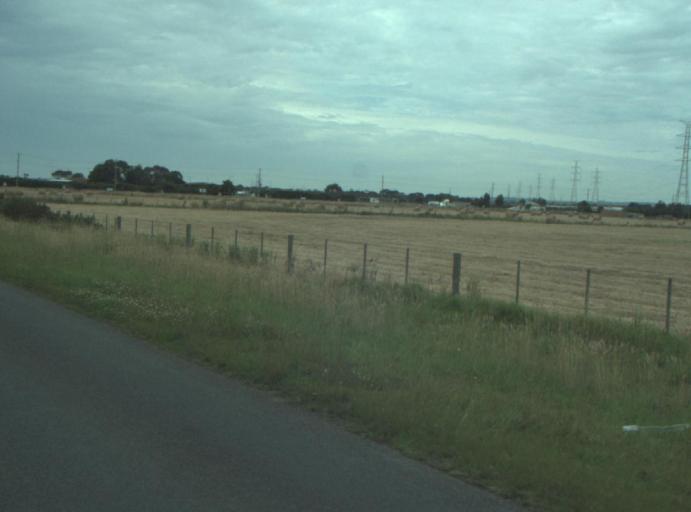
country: AU
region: Victoria
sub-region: Greater Geelong
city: Leopold
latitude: -38.1815
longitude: 144.4197
